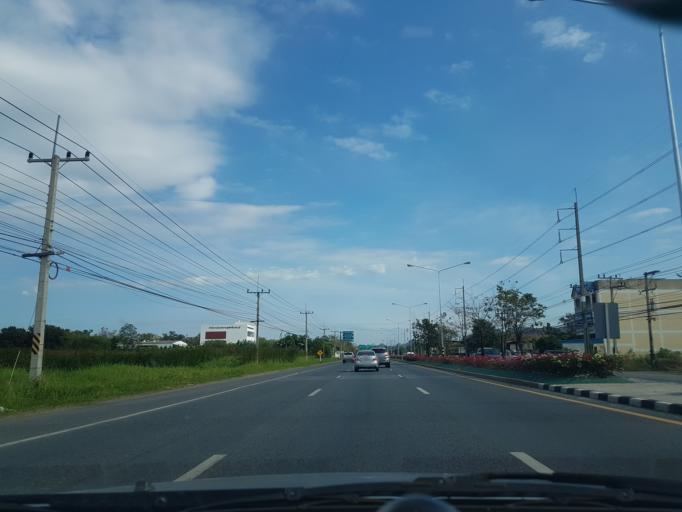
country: TH
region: Sara Buri
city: Phra Phutthabat
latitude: 14.7378
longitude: 100.7714
